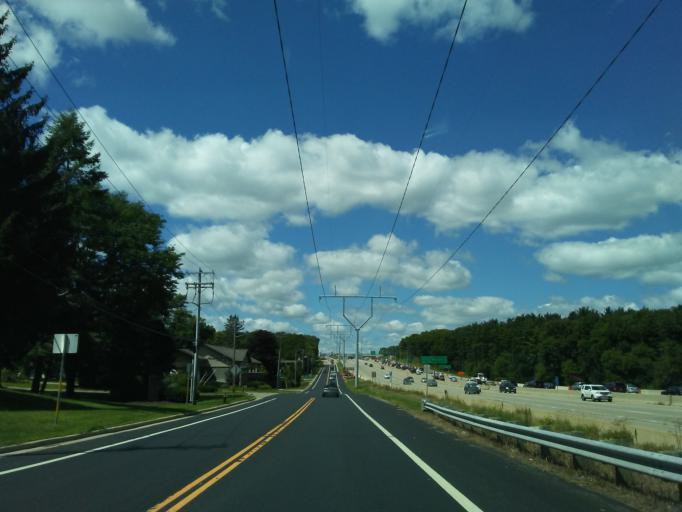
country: US
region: Wisconsin
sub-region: Dane County
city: Shorewood Hills
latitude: 43.0352
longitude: -89.4324
